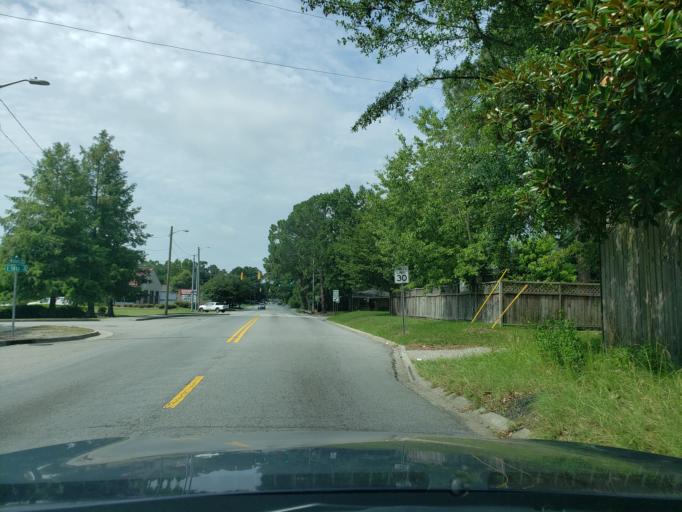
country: US
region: Georgia
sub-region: Chatham County
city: Thunderbolt
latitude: 32.0372
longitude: -81.0899
